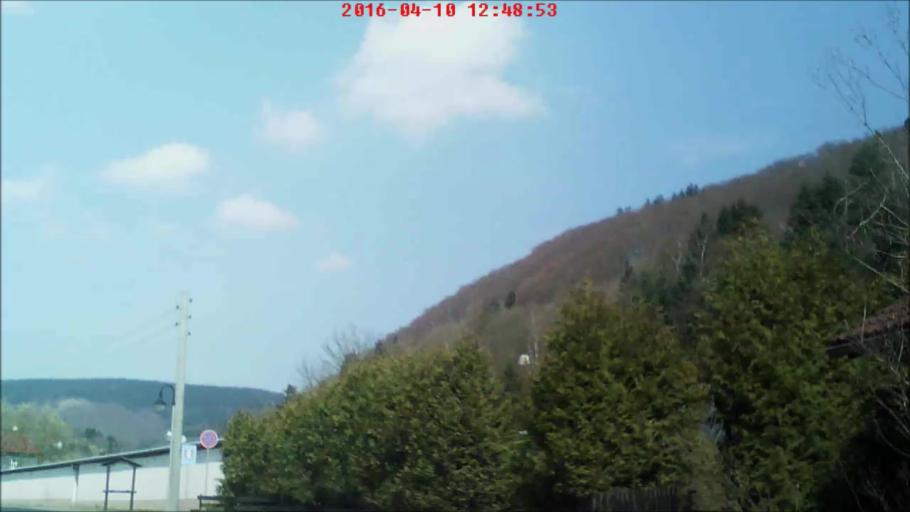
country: DE
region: Thuringia
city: Pappenheim
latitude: 50.7907
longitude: 10.4746
